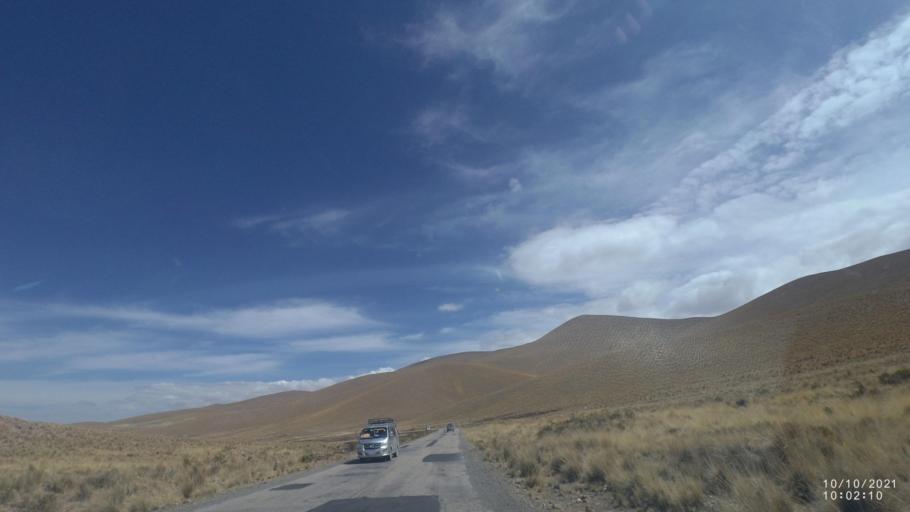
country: BO
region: La Paz
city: Eucaliptus
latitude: -17.3629
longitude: -67.4306
